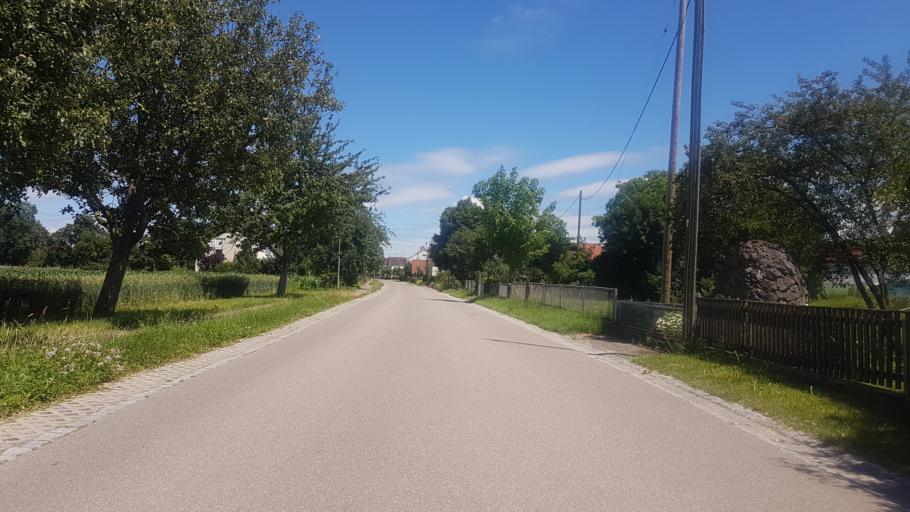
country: DE
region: Bavaria
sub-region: Swabia
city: Schwenningen
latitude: 48.6350
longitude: 10.6406
